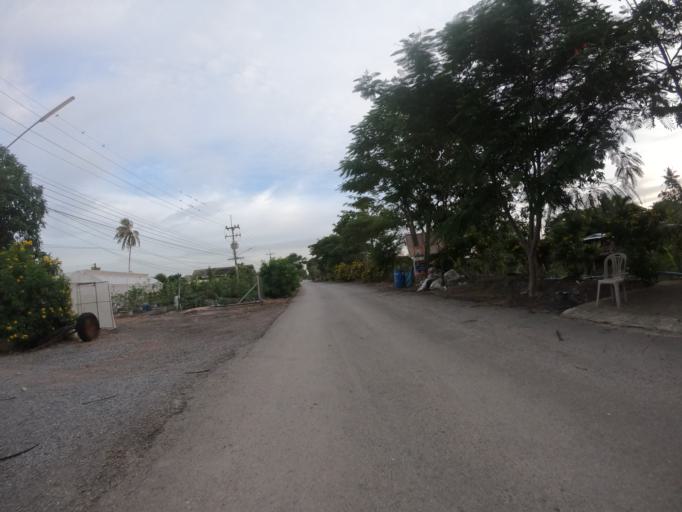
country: TH
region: Pathum Thani
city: Ban Lam Luk Ka
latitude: 14.0130
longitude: 100.7992
